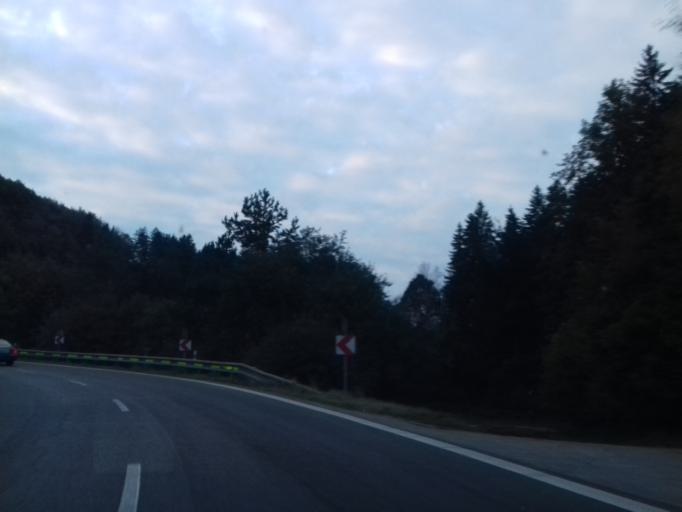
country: CZ
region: Zlin
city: Bojkovice
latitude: 48.9755
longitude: 17.8579
